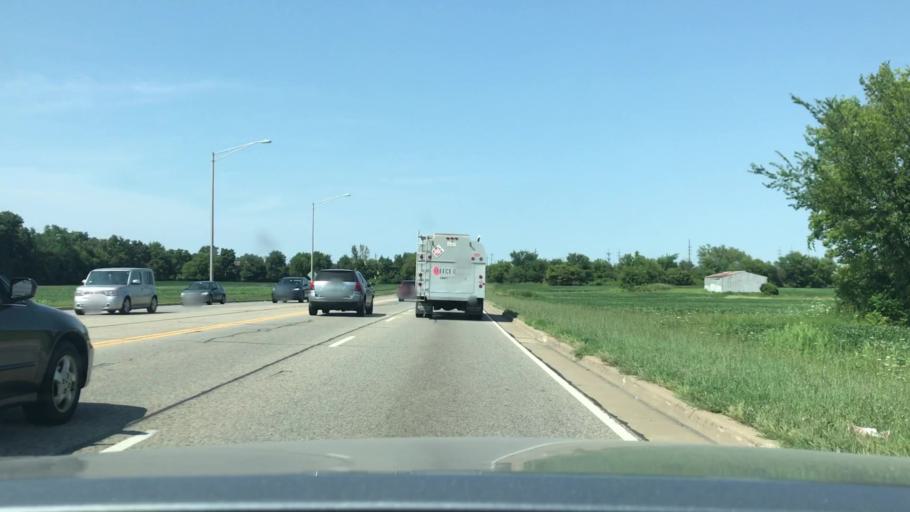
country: US
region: Illinois
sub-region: Kane County
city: Batavia
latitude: 41.8247
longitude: -88.2798
